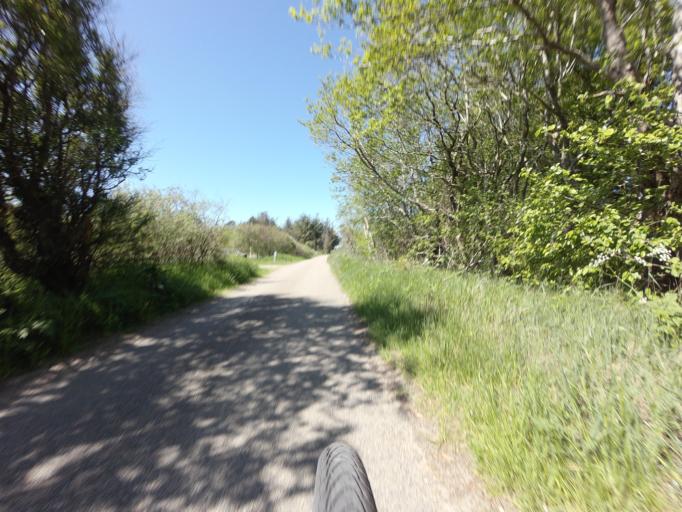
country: DK
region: North Denmark
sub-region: Jammerbugt Kommune
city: Pandrup
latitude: 57.2920
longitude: 9.6440
